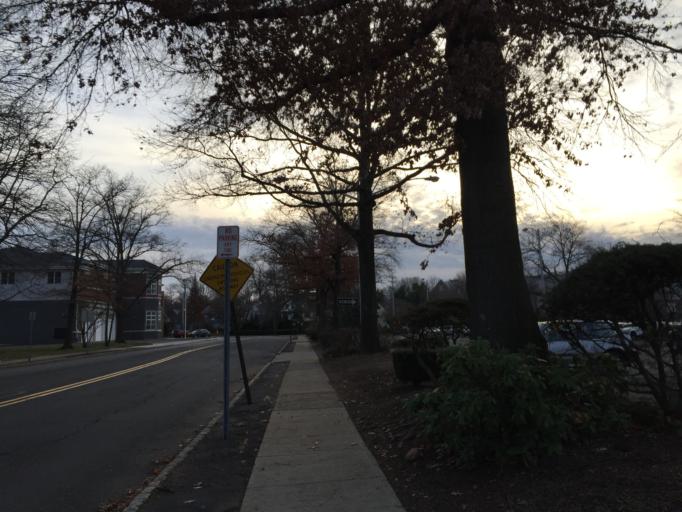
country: US
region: New Jersey
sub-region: Union County
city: Summit
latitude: 40.7133
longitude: -74.3581
